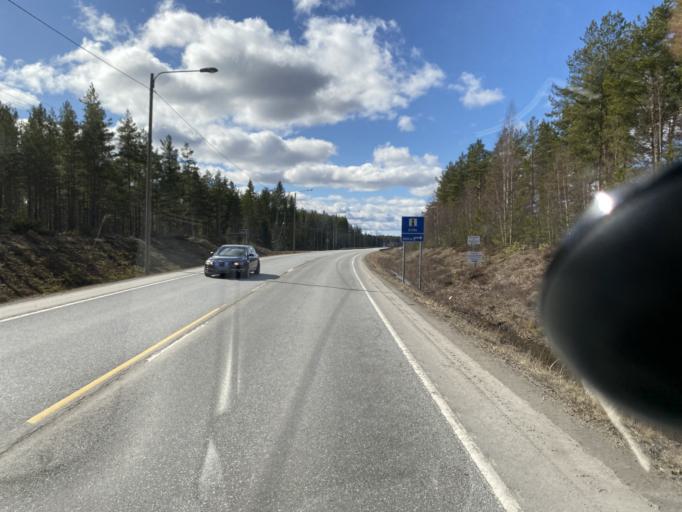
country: FI
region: Satakunta
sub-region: Rauma
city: Eura
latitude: 61.1394
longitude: 22.1836
